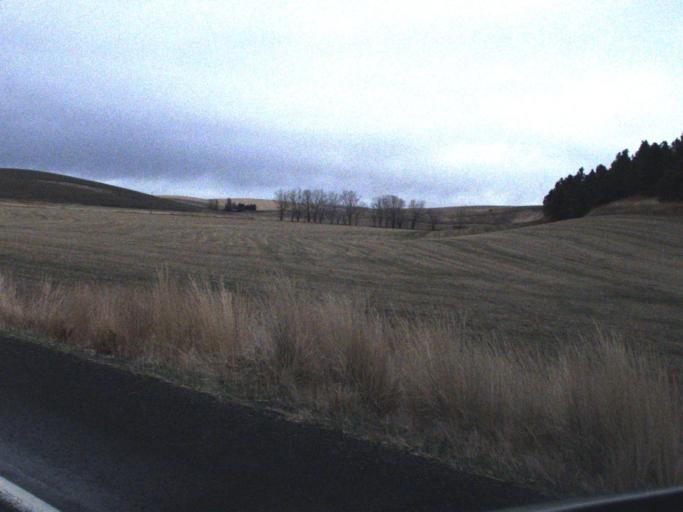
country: US
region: Washington
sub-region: Columbia County
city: Dayton
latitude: 46.3800
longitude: -117.9393
